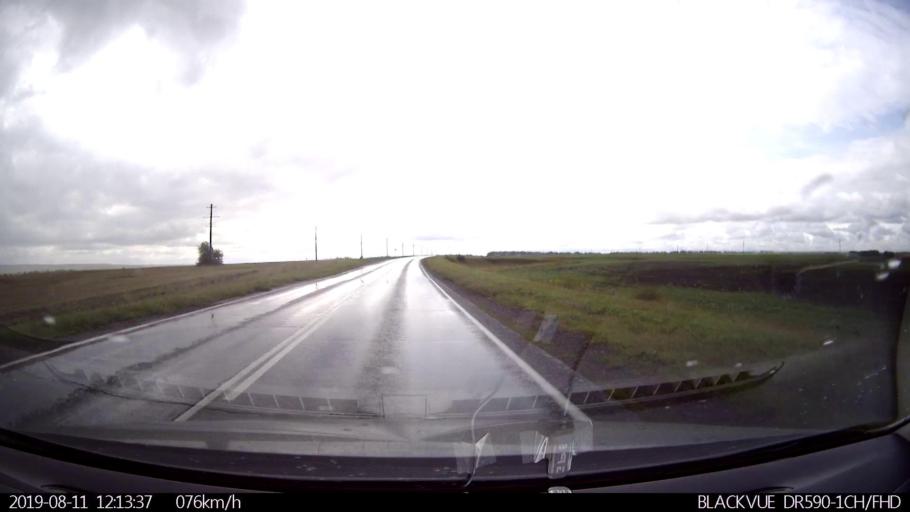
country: RU
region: Ulyanovsk
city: Ignatovka
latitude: 53.9602
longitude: 47.9906
